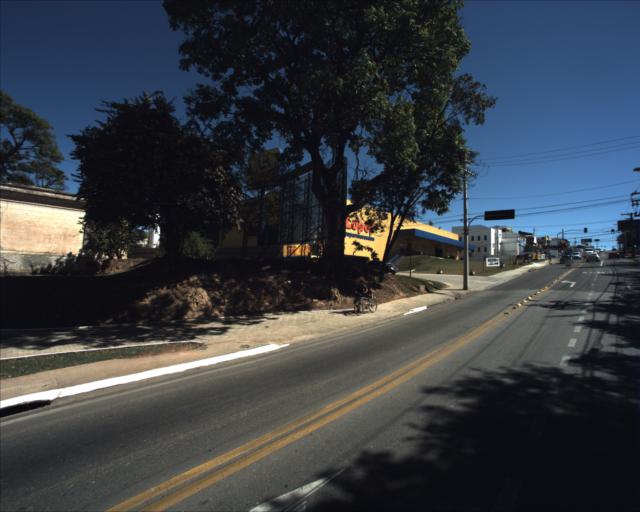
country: BR
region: Sao Paulo
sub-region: Sorocaba
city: Sorocaba
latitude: -23.5022
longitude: -47.5000
